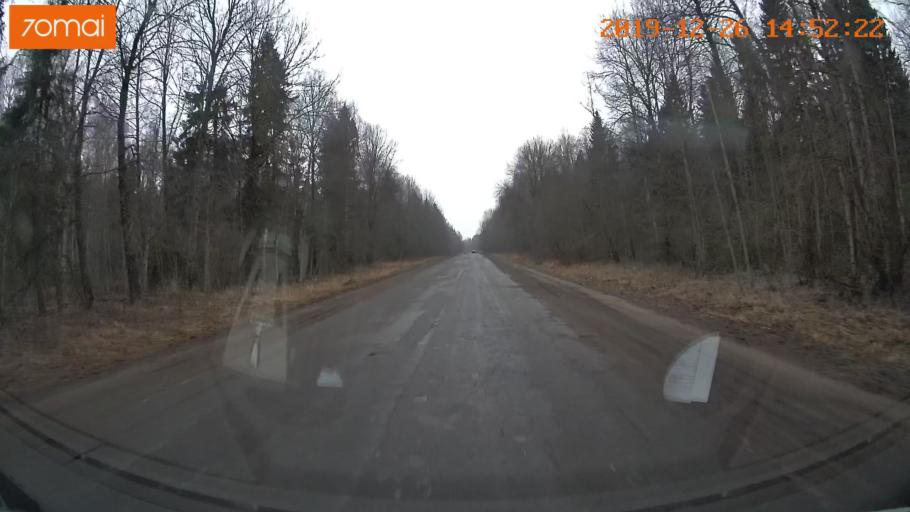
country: RU
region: Jaroslavl
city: Rybinsk
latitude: 58.3220
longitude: 38.8994
